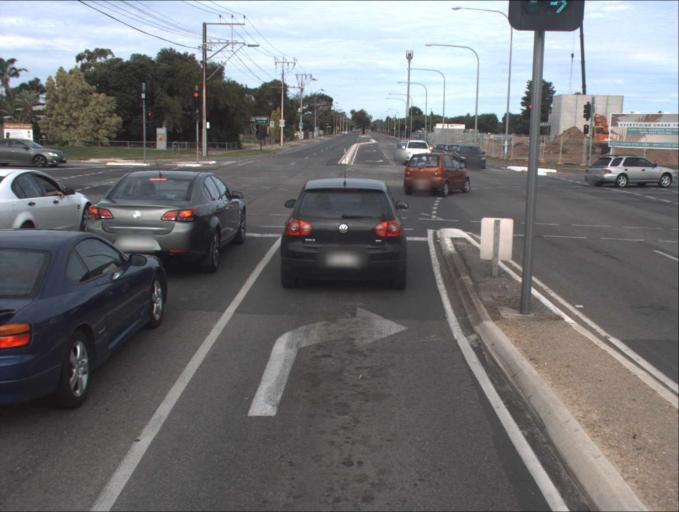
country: AU
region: South Australia
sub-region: Charles Sturt
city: Royal Park
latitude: -34.8795
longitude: 138.5037
